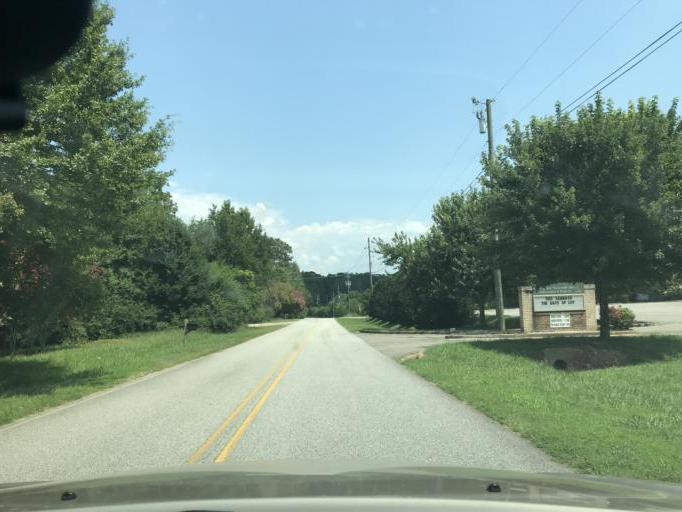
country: US
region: Georgia
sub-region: Dawson County
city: Dawsonville
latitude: 34.3373
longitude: -84.0762
